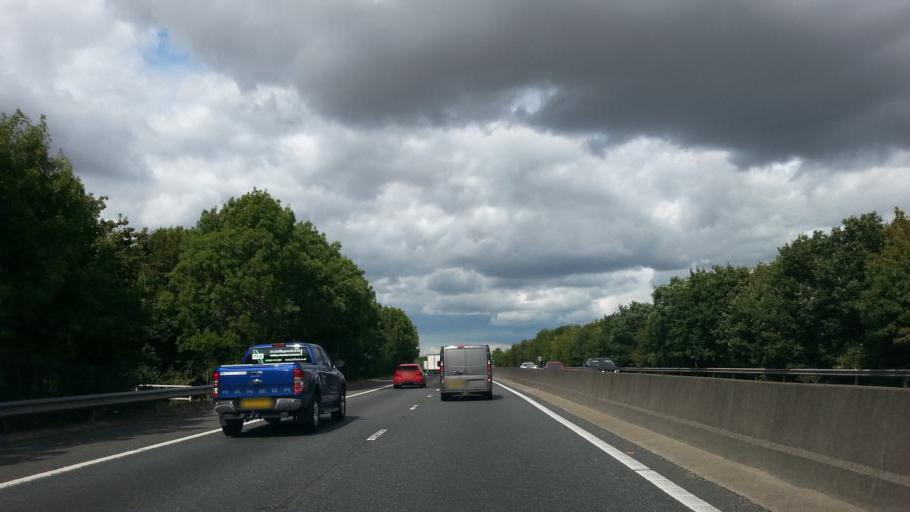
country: GB
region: England
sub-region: Essex
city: Elsenham
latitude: 51.9499
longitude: 0.2159
